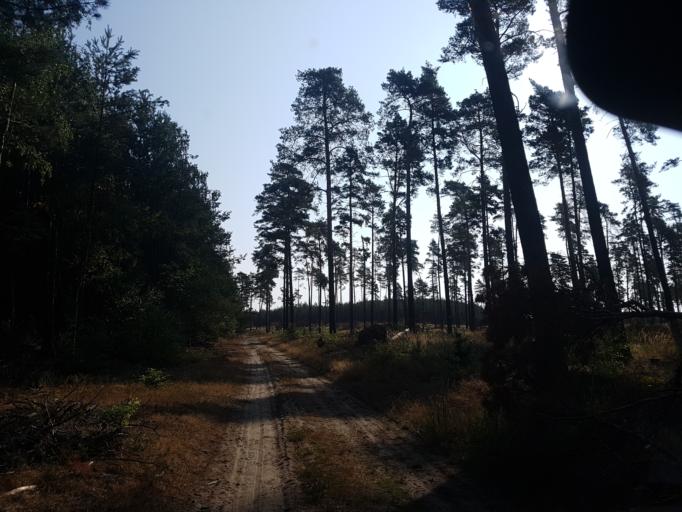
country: DE
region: Brandenburg
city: Gorzke
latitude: 52.0632
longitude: 12.3395
